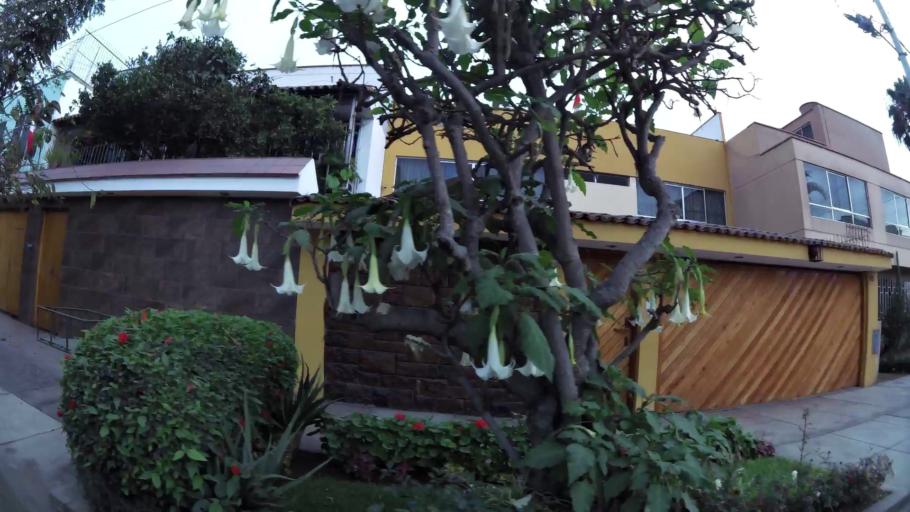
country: PE
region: Lima
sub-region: Lima
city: San Isidro
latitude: -12.1069
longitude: -77.0558
